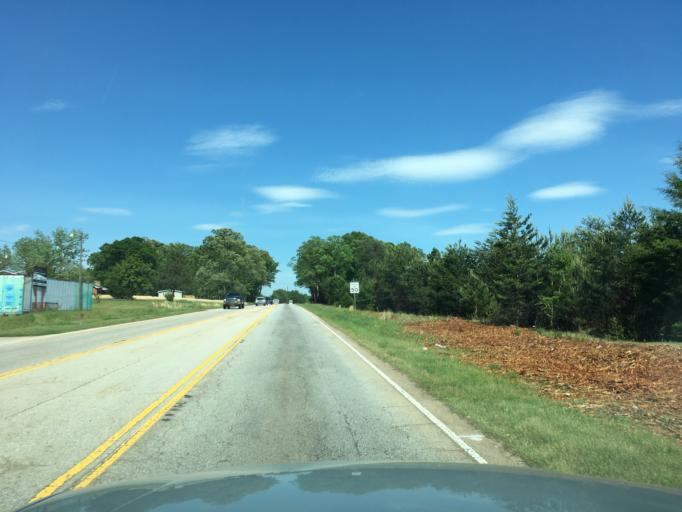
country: US
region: South Carolina
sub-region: Spartanburg County
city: Wellford
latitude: 34.9606
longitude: -82.0713
